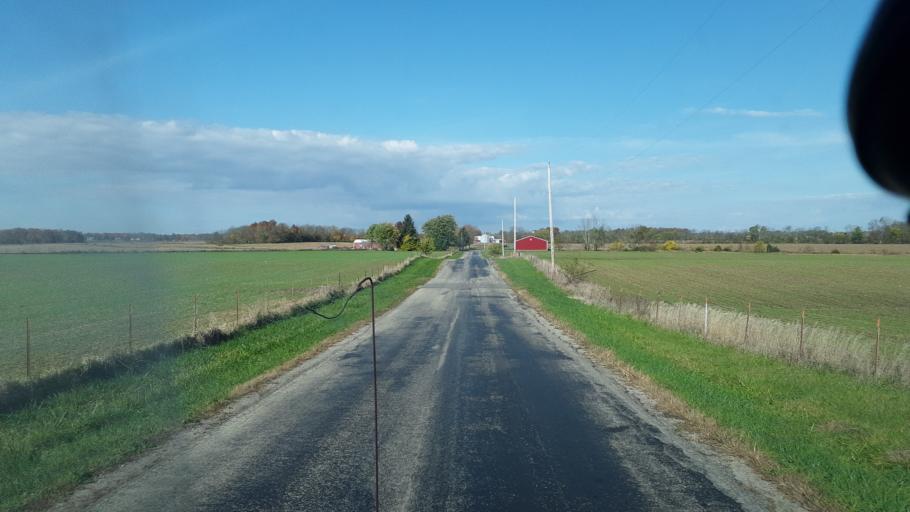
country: US
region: Ohio
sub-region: Highland County
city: Leesburg
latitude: 39.2777
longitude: -83.5669
